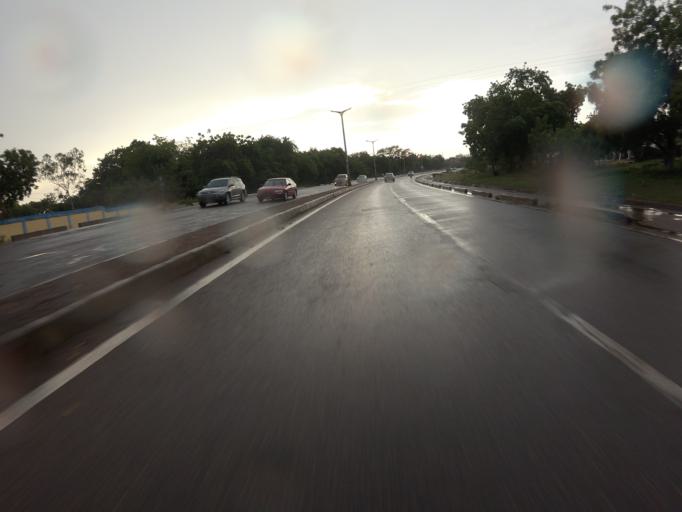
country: GH
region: Upper East
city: Bolgatanga
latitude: 10.8015
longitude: -0.8622
